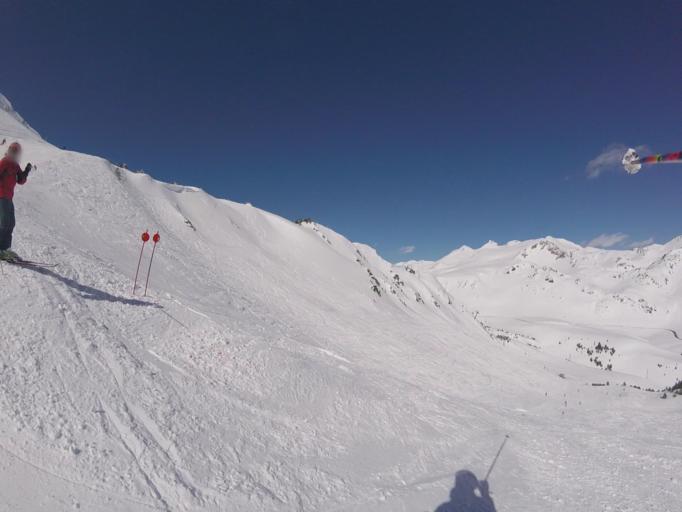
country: ES
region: Catalonia
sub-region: Provincia de Lleida
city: Espot
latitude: 42.6489
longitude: 0.9903
